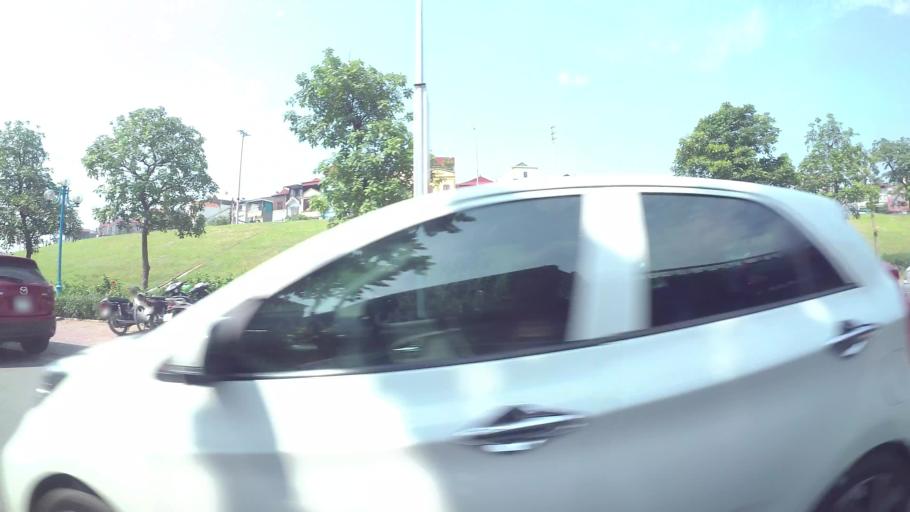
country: VN
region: Ha Noi
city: Hoan Kiem
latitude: 21.0508
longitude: 105.8648
